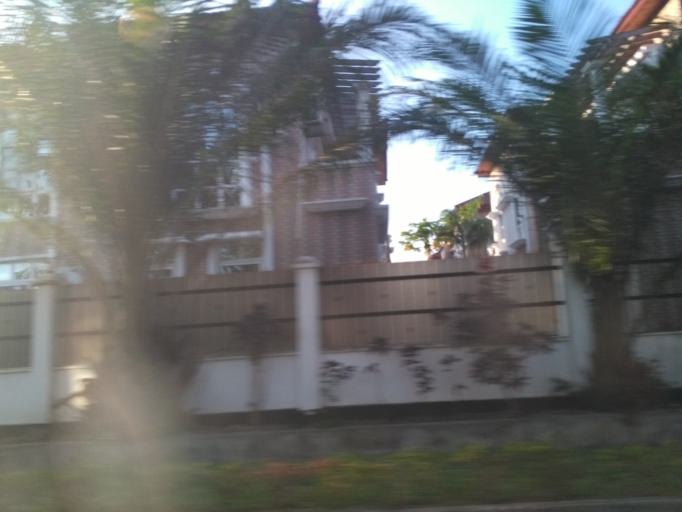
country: TZ
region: Dar es Salaam
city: Magomeni
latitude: -6.7655
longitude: 39.2631
